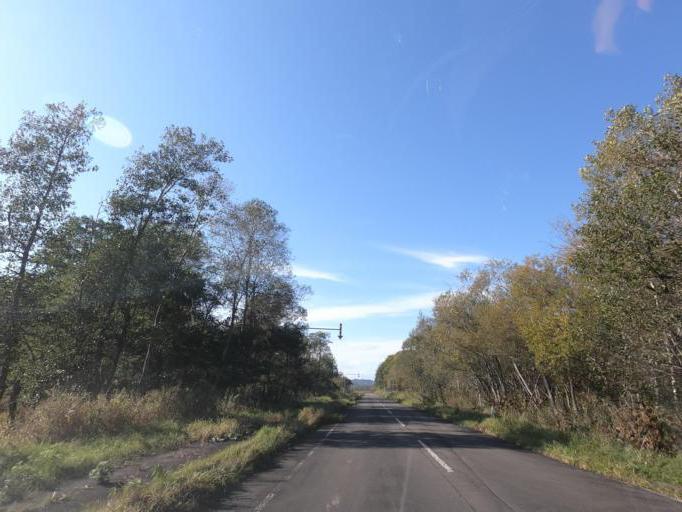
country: JP
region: Hokkaido
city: Obihiro
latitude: 42.6284
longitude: 143.5284
